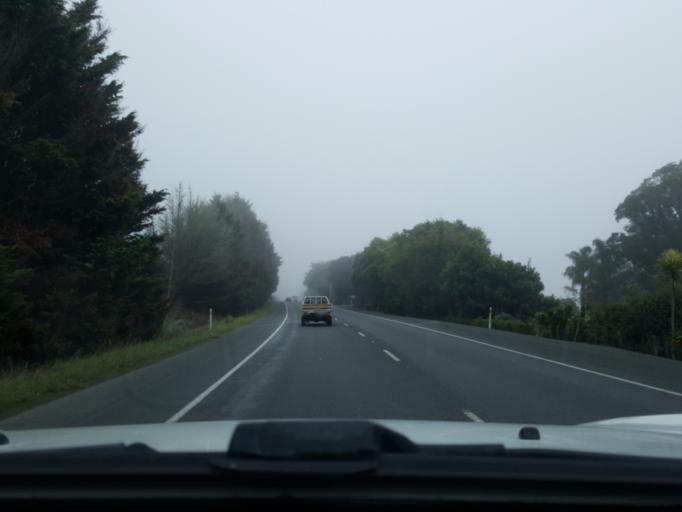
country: NZ
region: Waikato
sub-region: Waikato District
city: Ngaruawahia
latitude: -37.6943
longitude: 175.1897
